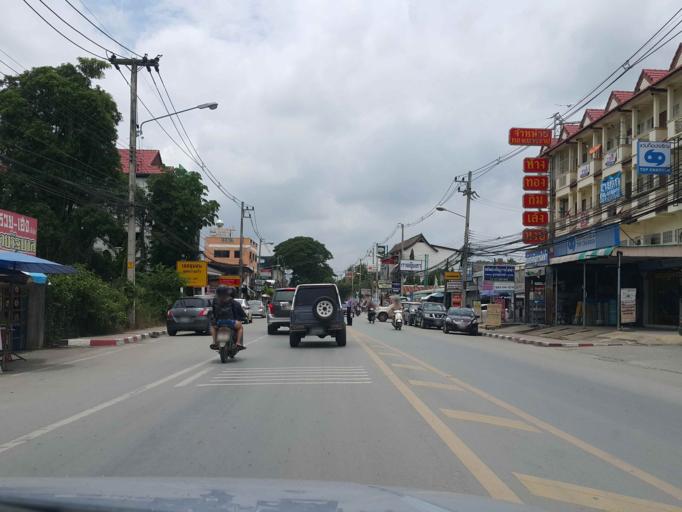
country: TH
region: Chiang Mai
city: San Kamphaeng
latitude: 18.7653
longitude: 99.0791
